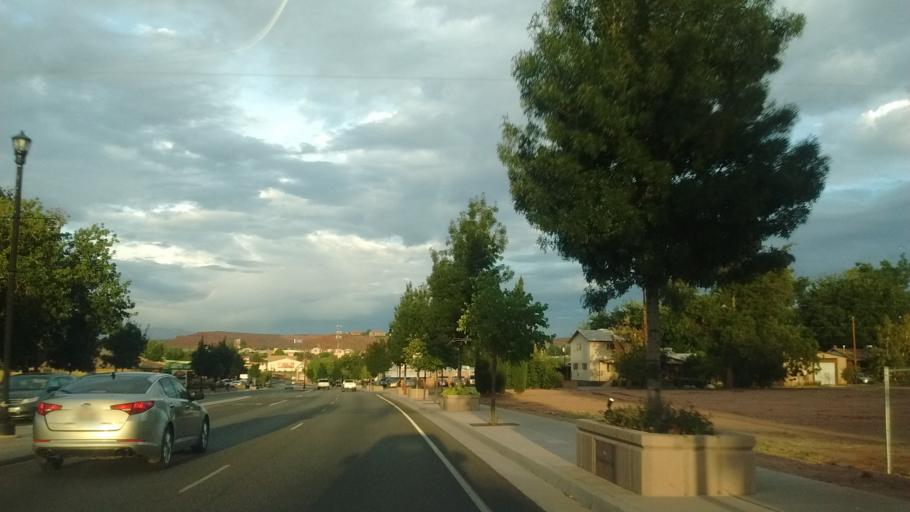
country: US
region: Utah
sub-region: Washington County
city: Washington
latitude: 37.1304
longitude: -113.5106
